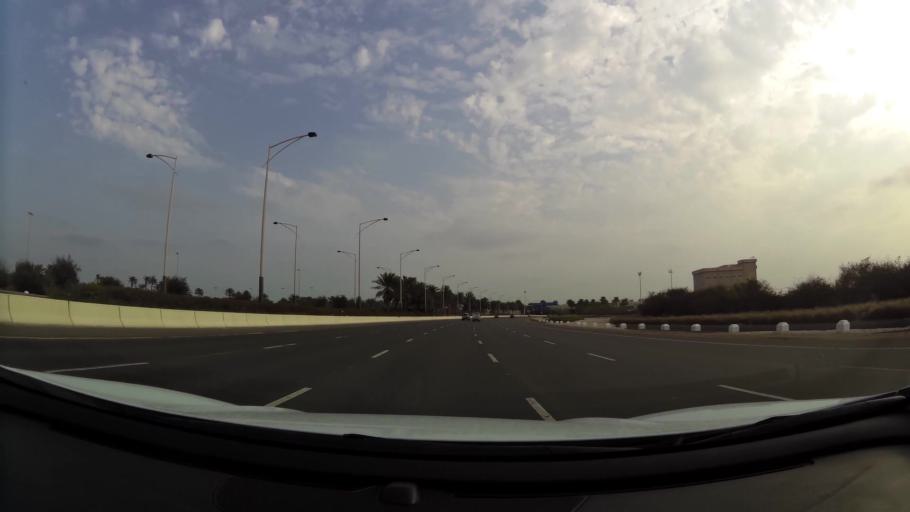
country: AE
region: Abu Dhabi
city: Abu Dhabi
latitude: 24.5393
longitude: 54.4377
